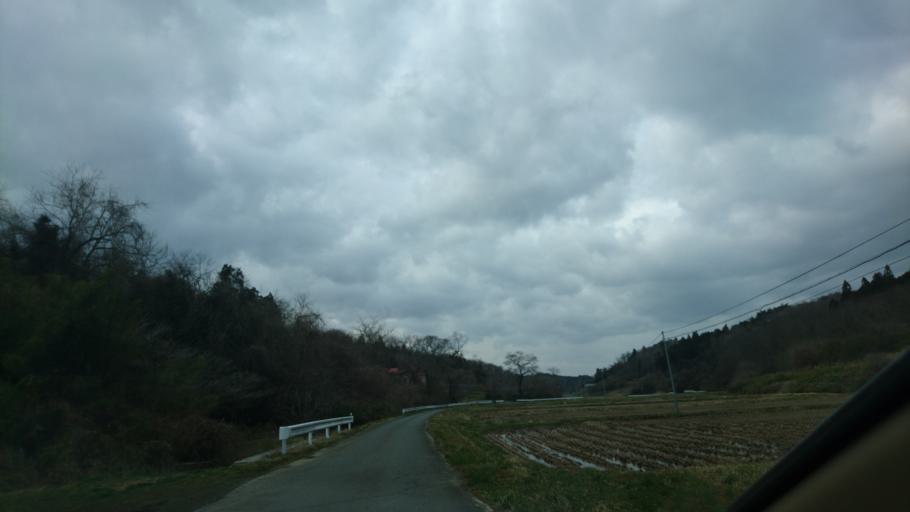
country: JP
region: Iwate
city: Ichinoseki
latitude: 38.8934
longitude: 141.1840
